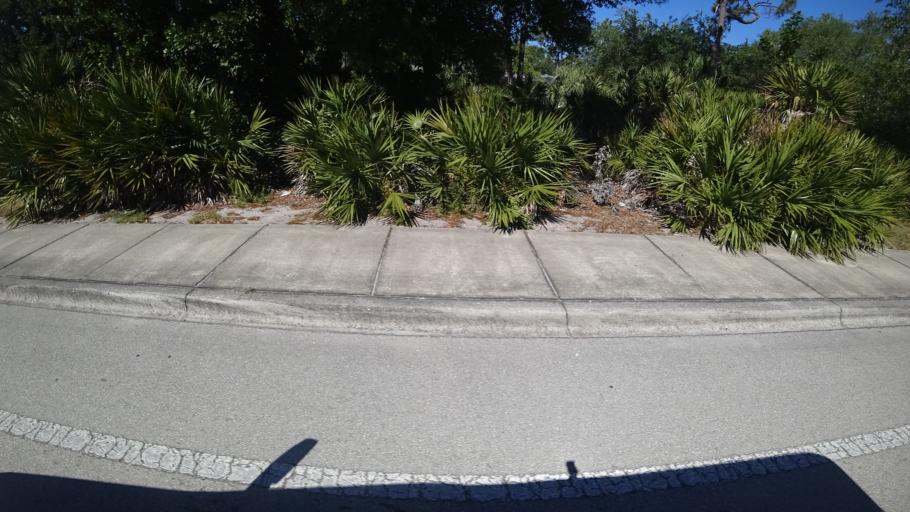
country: US
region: Florida
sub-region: Manatee County
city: West Bradenton
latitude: 27.4743
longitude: -82.6369
